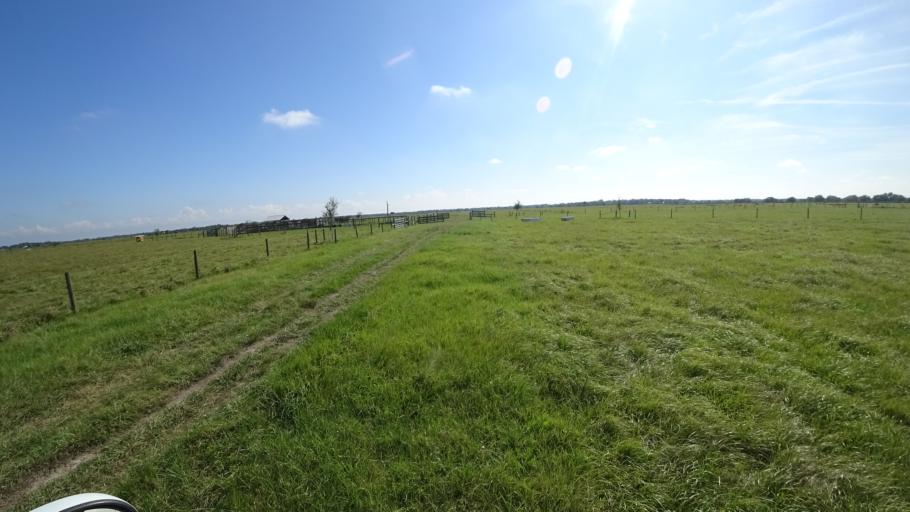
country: US
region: Florida
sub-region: DeSoto County
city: Nocatee
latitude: 27.2671
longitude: -82.1003
